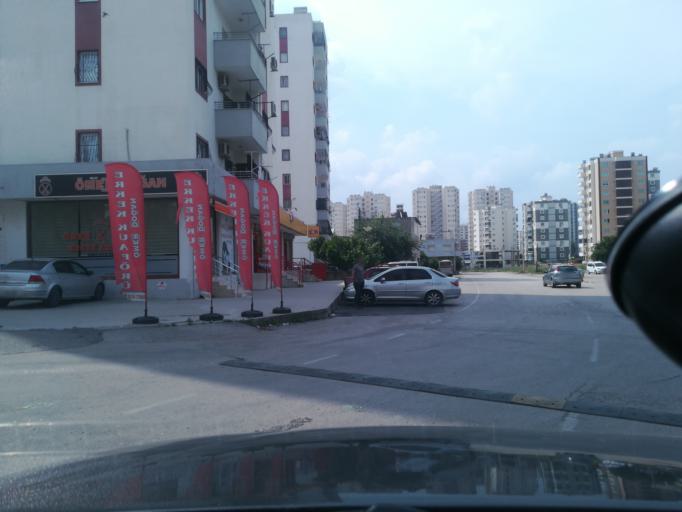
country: TR
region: Adana
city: Seyhan
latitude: 37.0275
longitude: 35.2805
